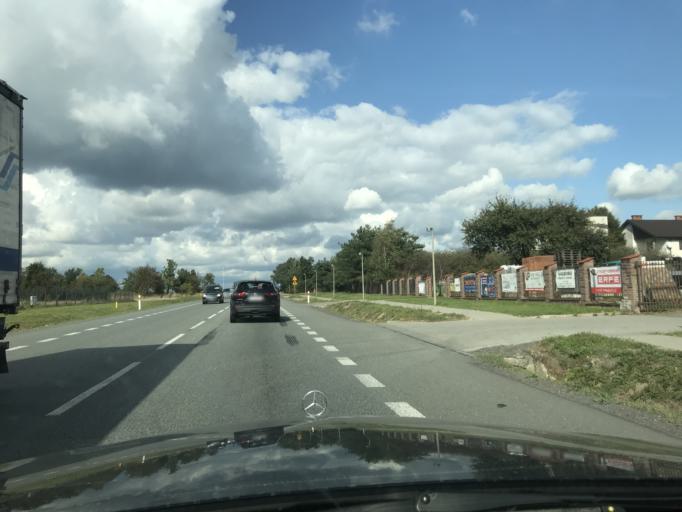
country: PL
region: Lublin Voivodeship
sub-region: Powiat lubelski
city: Niemce
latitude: 51.3463
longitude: 22.6195
